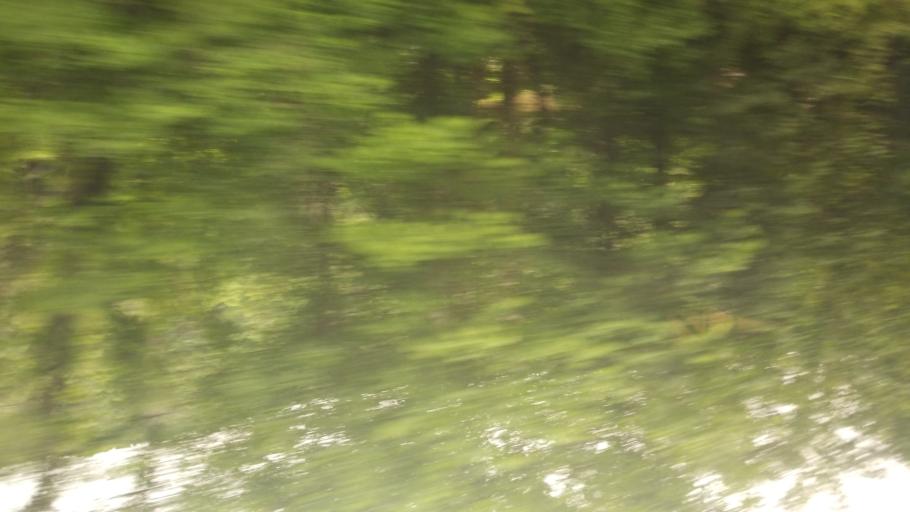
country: US
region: Pennsylvania
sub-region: Somerset County
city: Milford
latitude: 39.8487
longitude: -79.2319
